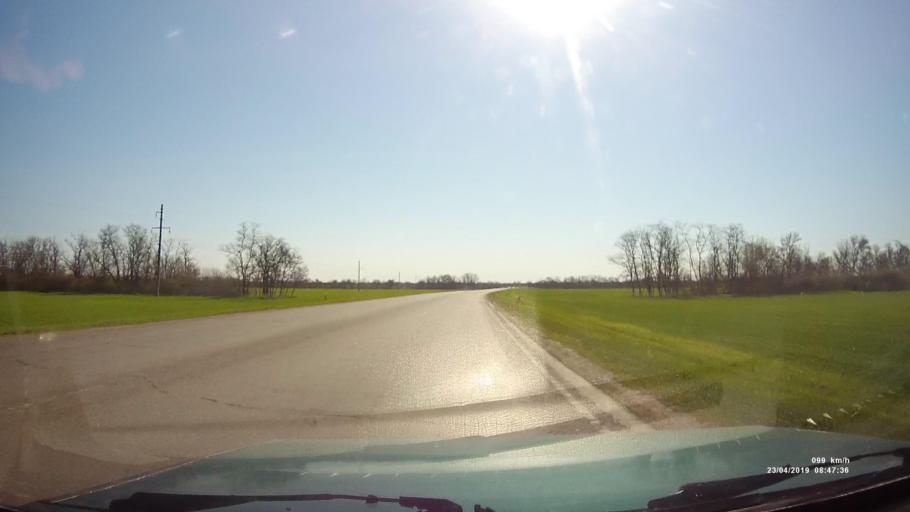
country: RU
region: Rostov
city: Gigant
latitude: 46.5147
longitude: 41.3742
